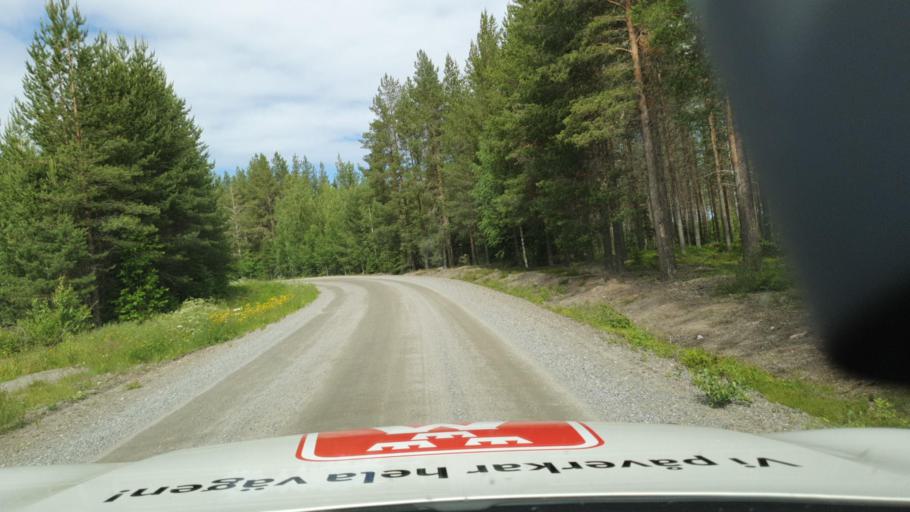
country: SE
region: Vaesterbotten
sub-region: Skelleftea Kommun
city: Burtraesk
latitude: 64.6129
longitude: 20.5931
